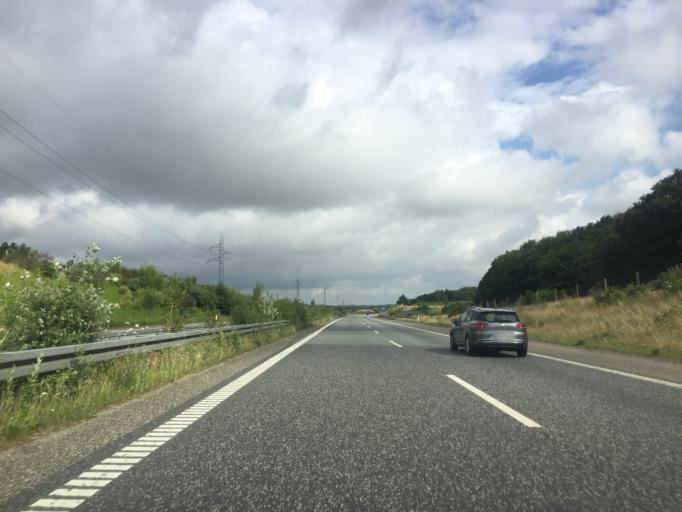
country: DK
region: South Denmark
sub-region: Svendborg Kommune
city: Svendborg
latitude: 55.1045
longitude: 10.5652
